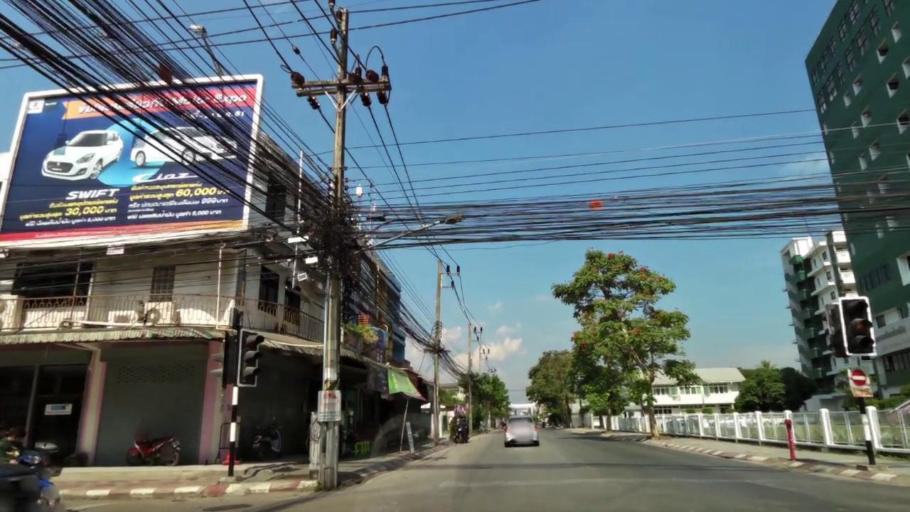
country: TH
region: Chiang Rai
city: Chiang Rai
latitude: 19.9021
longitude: 99.8282
